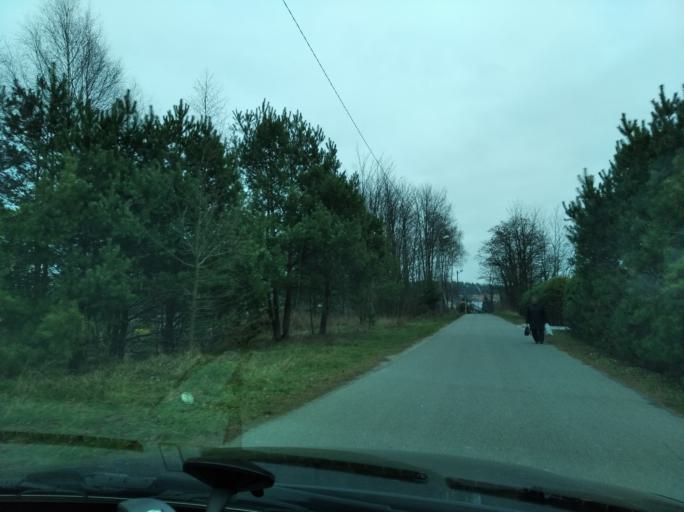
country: PL
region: Subcarpathian Voivodeship
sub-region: Powiat lancucki
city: Rakszawa
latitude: 50.1530
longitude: 22.2363
